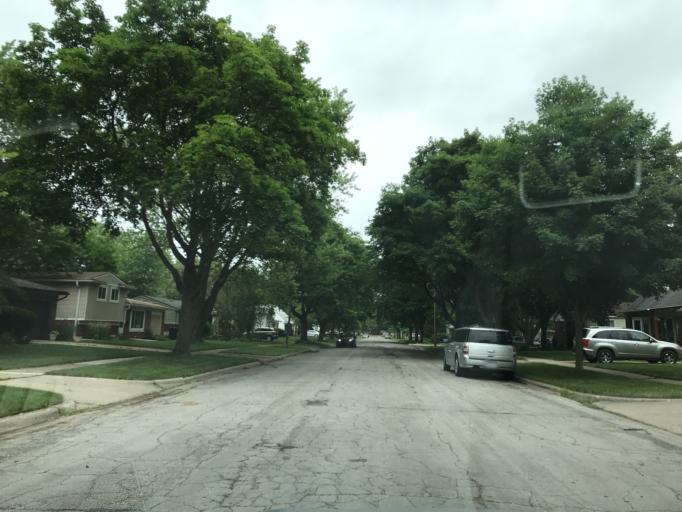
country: US
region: Michigan
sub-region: Washtenaw County
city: Ann Arbor
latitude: 42.2380
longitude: -83.7058
